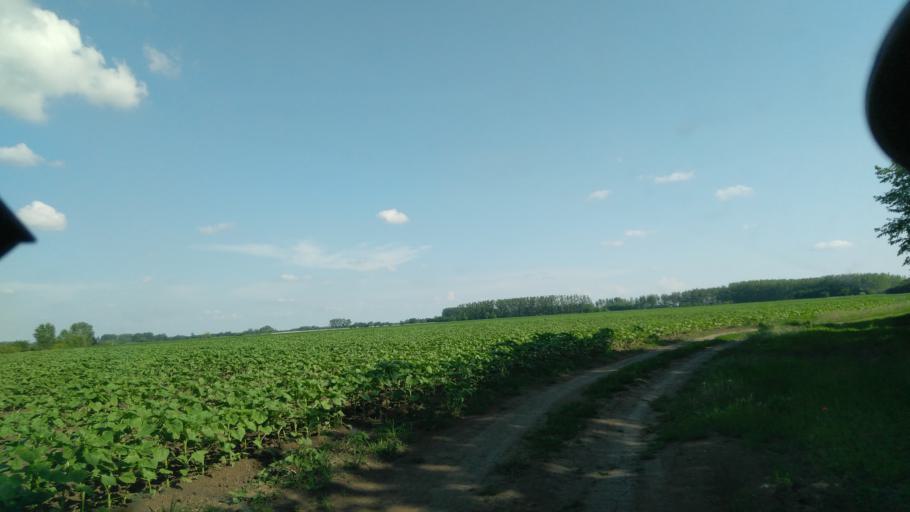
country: HU
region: Bekes
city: Doboz
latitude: 46.7078
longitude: 21.2347
